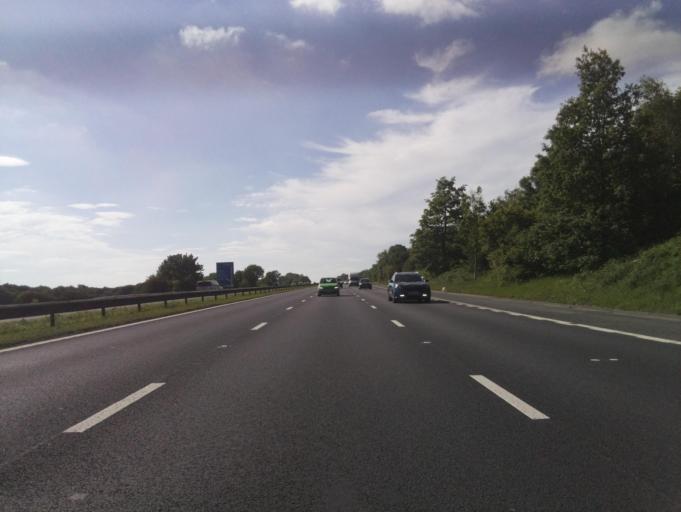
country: GB
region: England
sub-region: Borough of Wigan
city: Atherton
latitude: 53.5528
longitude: -2.4819
